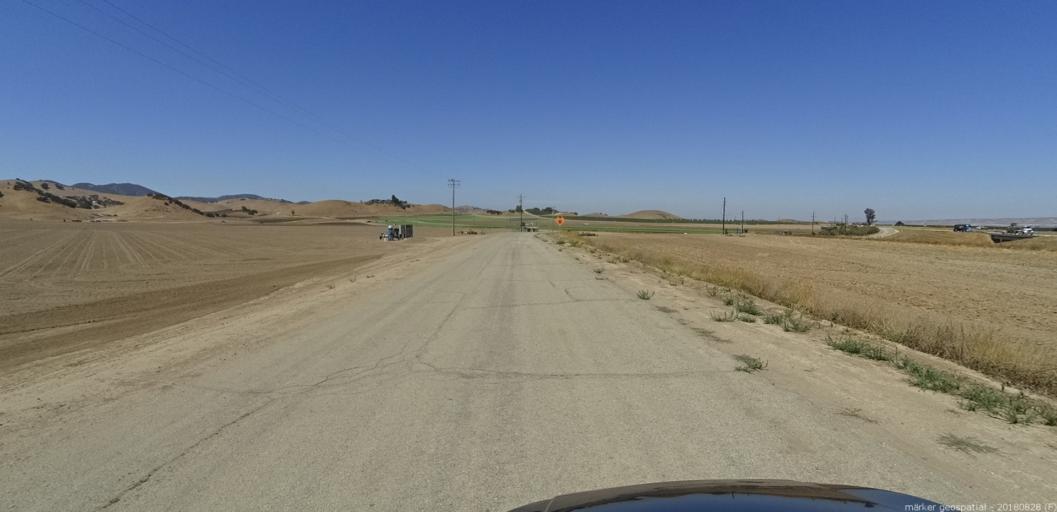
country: US
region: California
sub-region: San Luis Obispo County
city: Lake Nacimiento
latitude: 36.0107
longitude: -120.9218
